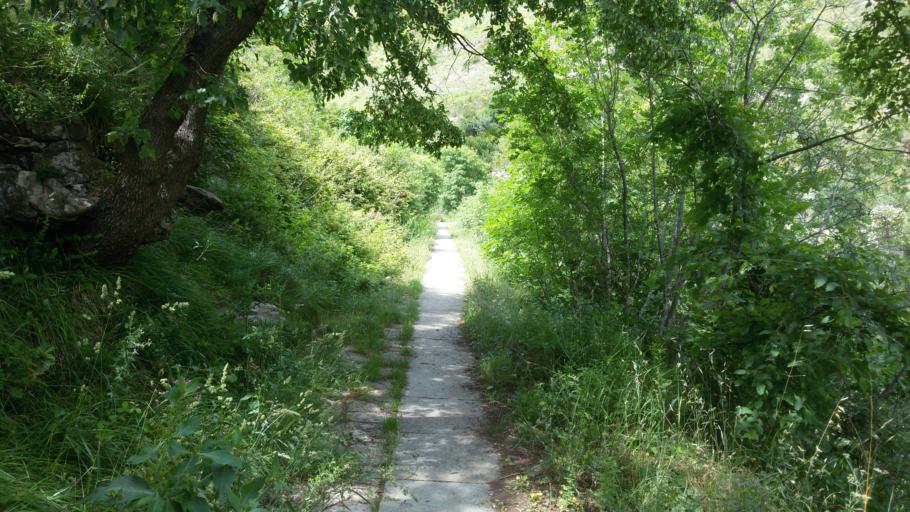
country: IT
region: Liguria
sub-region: Provincia di Genova
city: Piccarello
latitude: 44.4482
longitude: 8.9575
